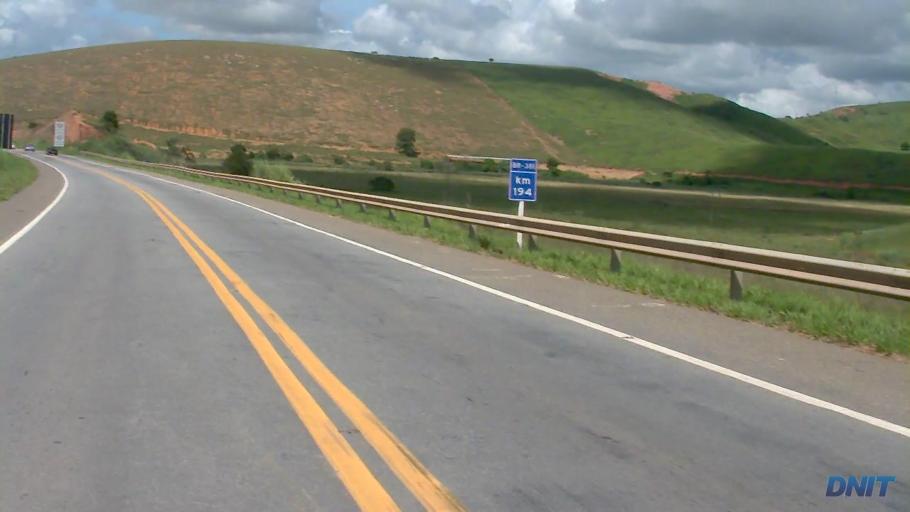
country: BR
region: Minas Gerais
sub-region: Belo Oriente
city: Belo Oriente
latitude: -19.1085
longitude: -42.2026
